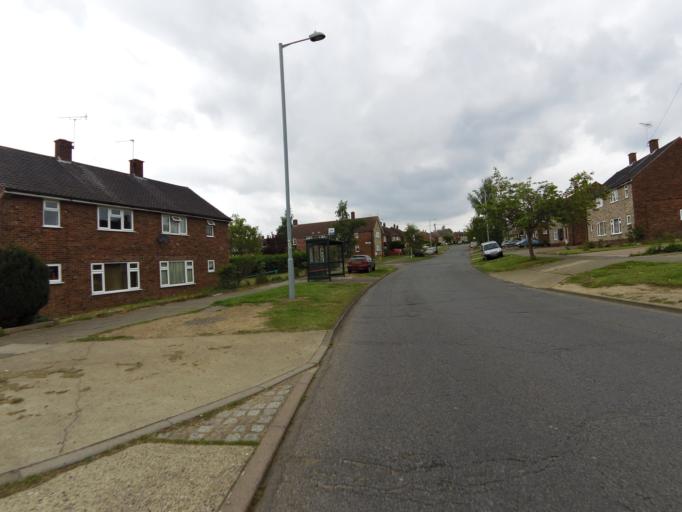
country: GB
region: England
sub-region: Suffolk
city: Ipswich
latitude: 52.0429
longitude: 1.1259
